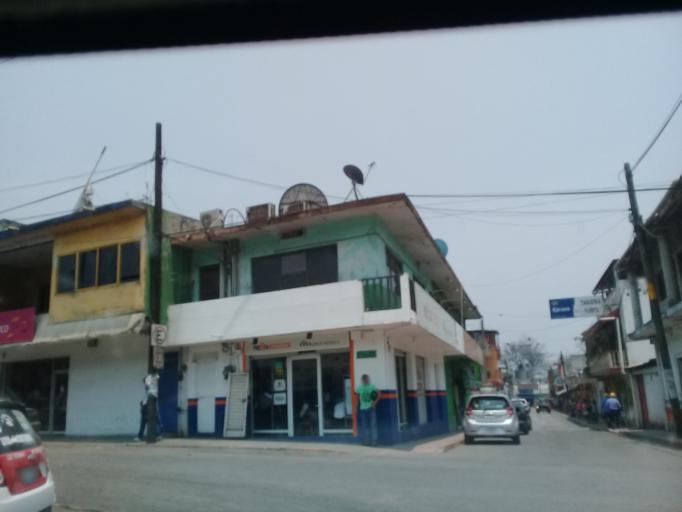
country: MX
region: Veracruz
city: Cosolapa
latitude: 18.6041
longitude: -96.6869
